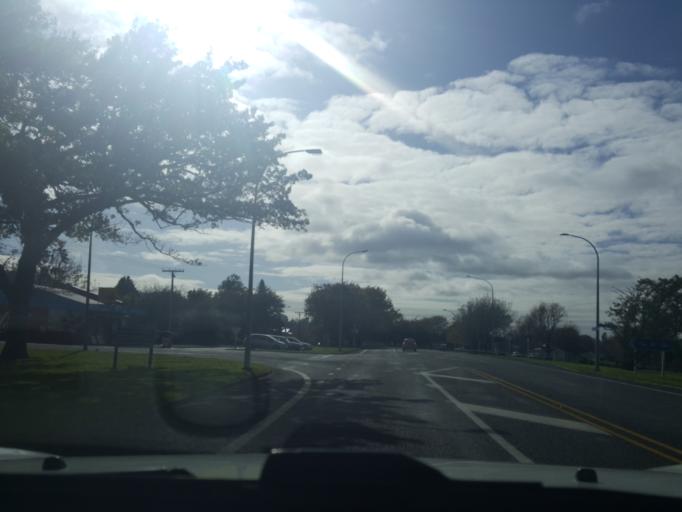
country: NZ
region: Waikato
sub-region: Hauraki District
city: Waihi
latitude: -37.3940
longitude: 175.8312
